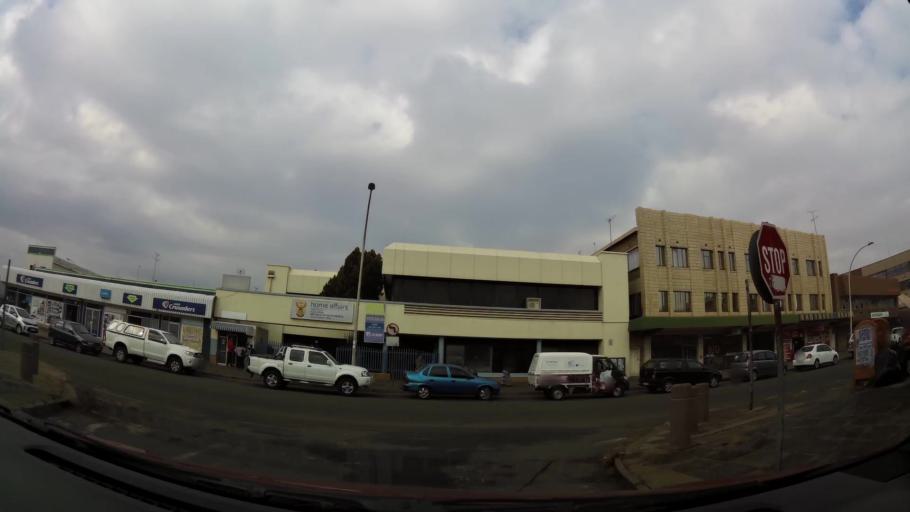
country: ZA
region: Gauteng
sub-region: Sedibeng District Municipality
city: Vanderbijlpark
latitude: -26.7003
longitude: 27.8372
